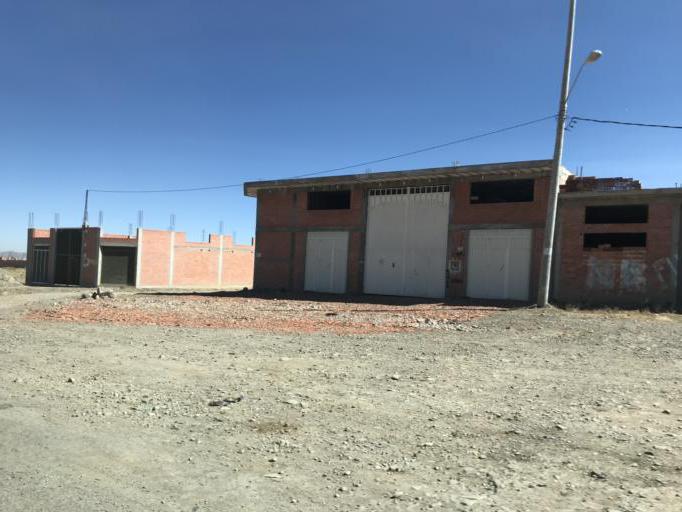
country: BO
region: La Paz
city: La Paz
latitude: -16.5095
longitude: -68.2674
